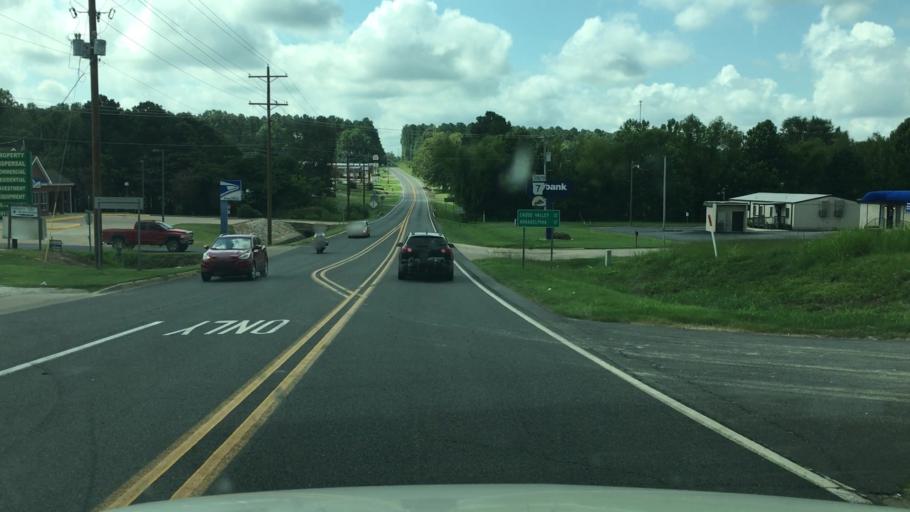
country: US
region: Arkansas
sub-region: Garland County
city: Lake Hamilton
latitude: 34.3161
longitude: -93.1709
